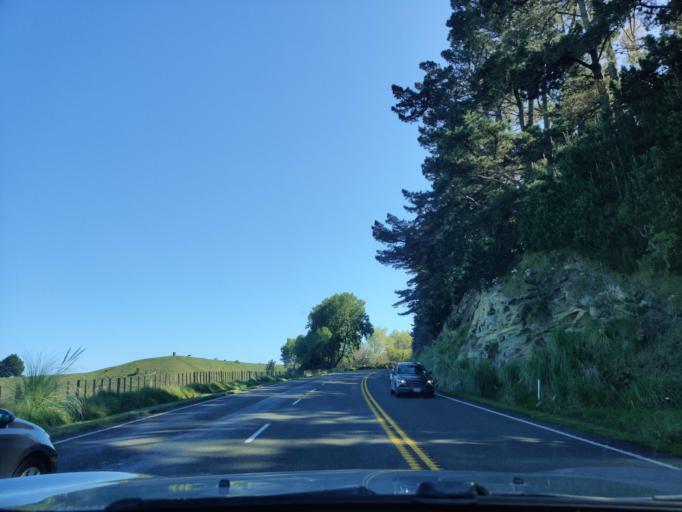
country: NZ
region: Manawatu-Wanganui
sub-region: Rangitikei District
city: Bulls
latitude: -40.0606
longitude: 175.2203
